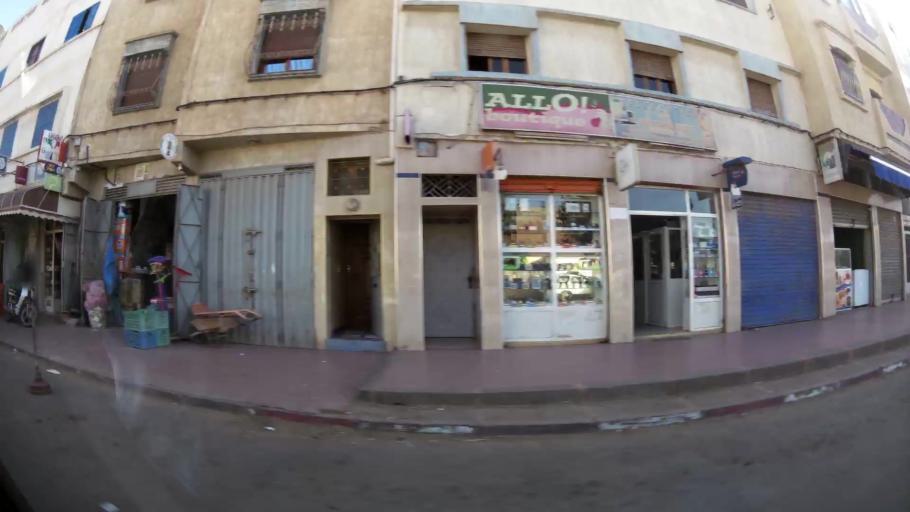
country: MA
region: Souss-Massa-Draa
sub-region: Inezgane-Ait Mellou
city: Inezgane
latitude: 30.3737
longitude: -9.5039
